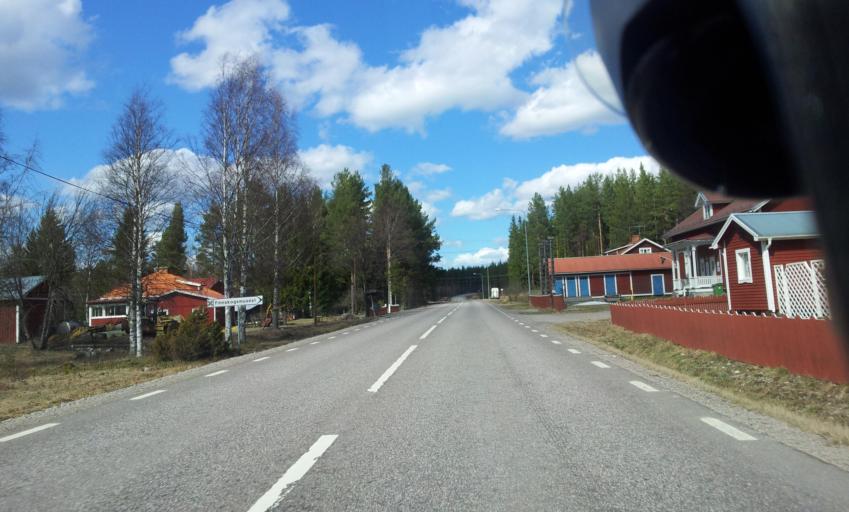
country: SE
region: Gaevleborg
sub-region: Ovanakers Kommun
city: Edsbyn
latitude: 61.2045
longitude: 15.8716
